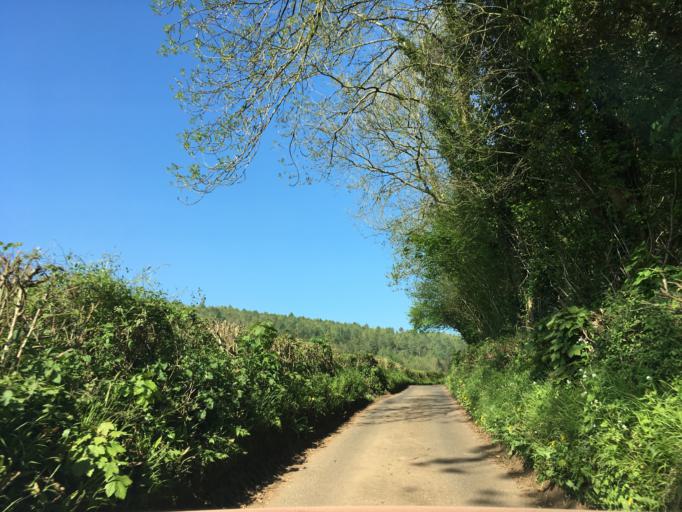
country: GB
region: Wales
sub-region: Newport
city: Llanvaches
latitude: 51.6276
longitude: -2.7935
